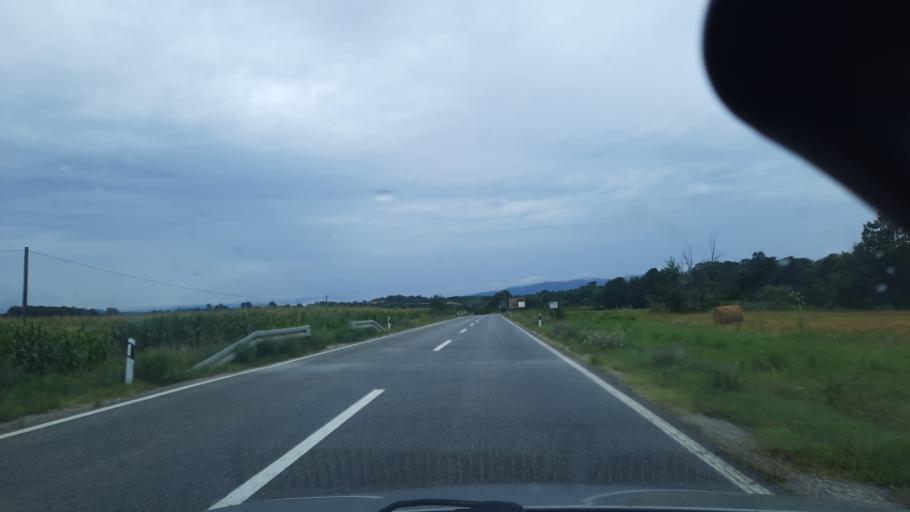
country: RS
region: Central Serbia
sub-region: Sumadijski Okrug
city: Knic
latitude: 43.9171
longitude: 20.7708
